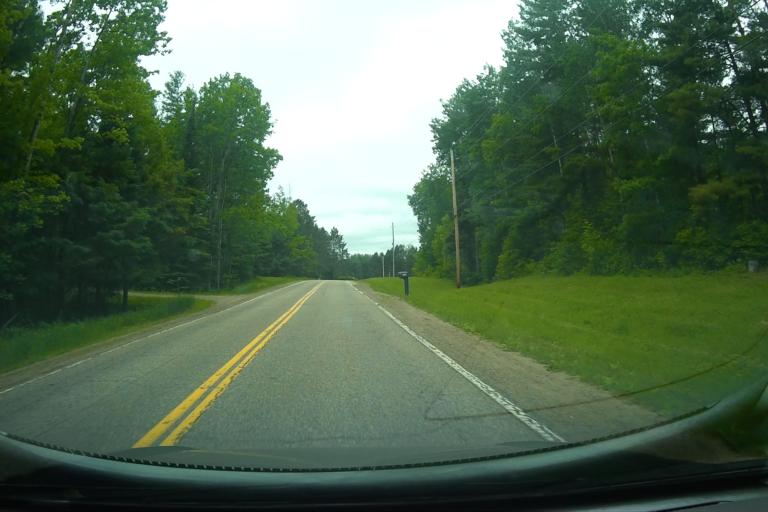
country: CA
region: Ontario
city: Pembroke
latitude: 45.4865
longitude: -77.2013
